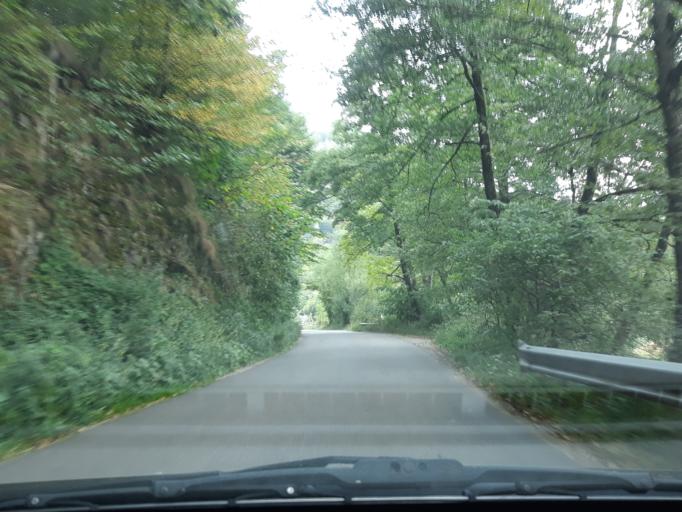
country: RO
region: Bihor
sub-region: Comuna Pietroasa
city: Pietroasa
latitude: 46.5894
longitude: 22.5842
